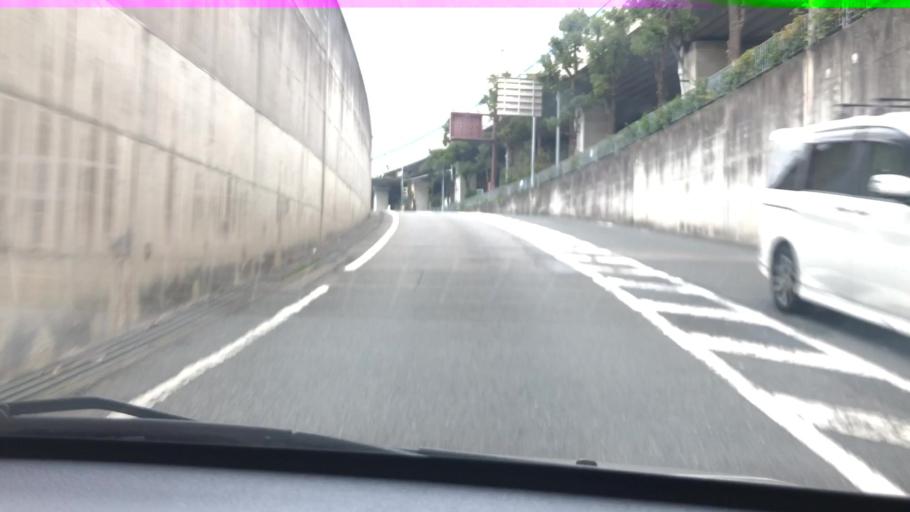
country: JP
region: Hyogo
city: Nishinomiya-hama
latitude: 34.7280
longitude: 135.3567
